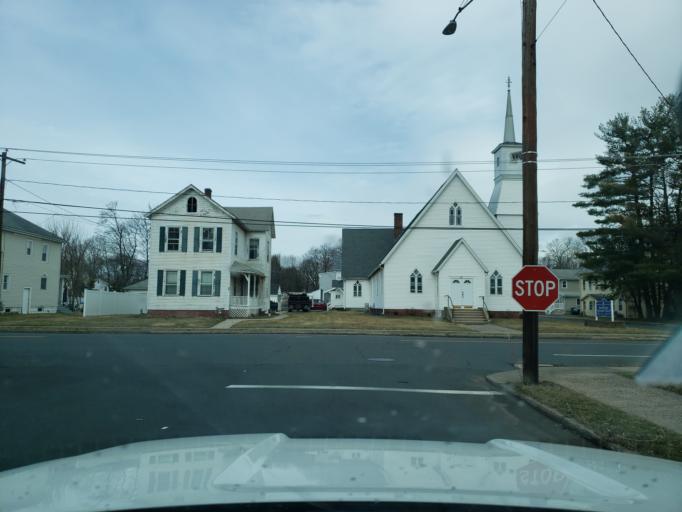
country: US
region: Connecticut
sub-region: Hartford County
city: Plainville
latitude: 41.6673
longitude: -72.8710
